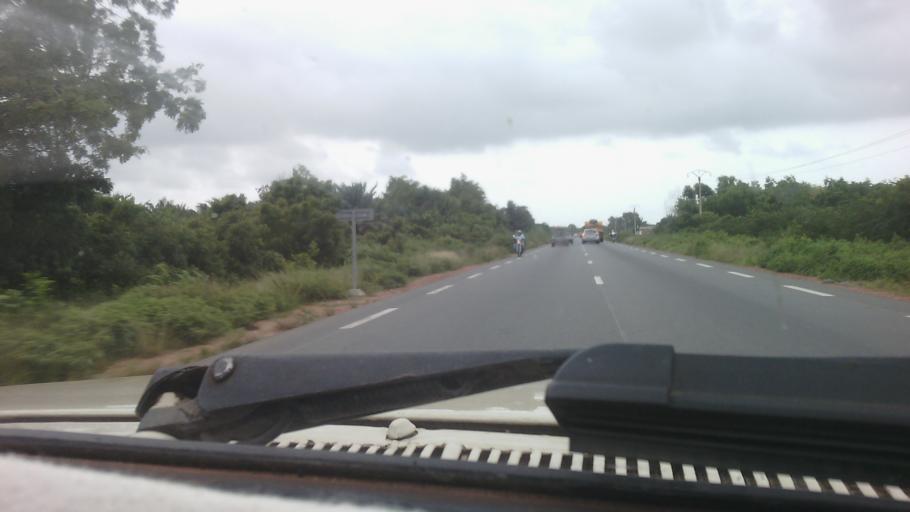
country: BJ
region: Atlantique
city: Ouidah
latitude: 6.3730
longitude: 2.0322
